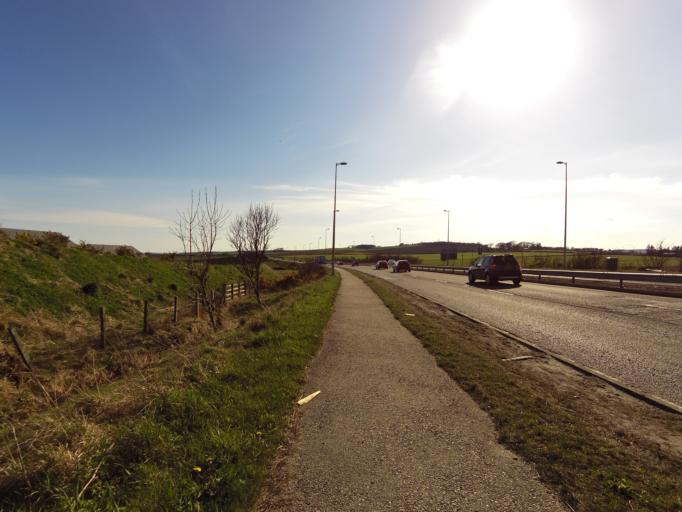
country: GB
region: Scotland
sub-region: Aberdeenshire
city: Newtonhill
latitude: 57.0286
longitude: -2.1638
